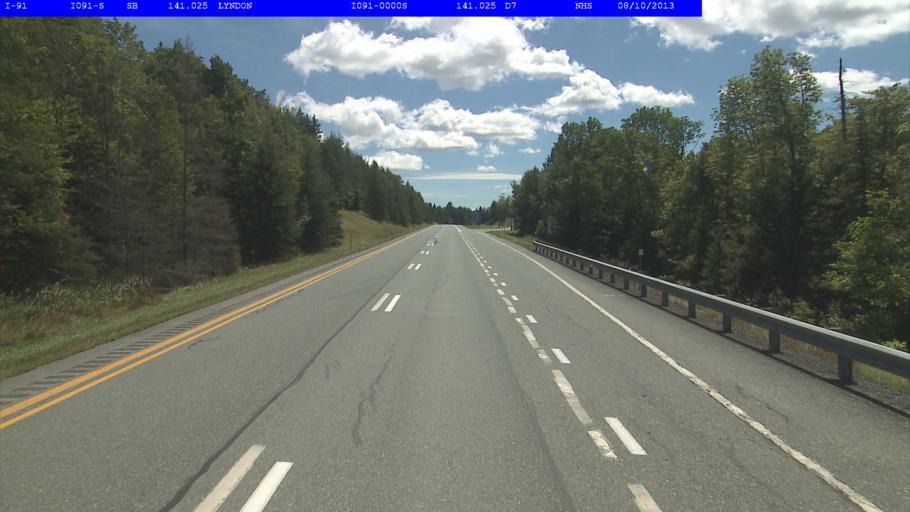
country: US
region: Vermont
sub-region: Caledonia County
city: Lyndonville
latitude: 44.5673
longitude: -72.0359
